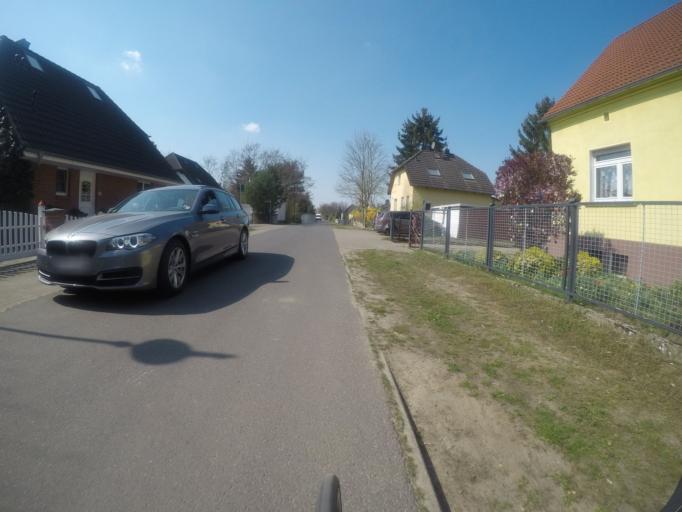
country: DE
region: Brandenburg
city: Brieselang
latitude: 52.6384
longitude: 13.0512
